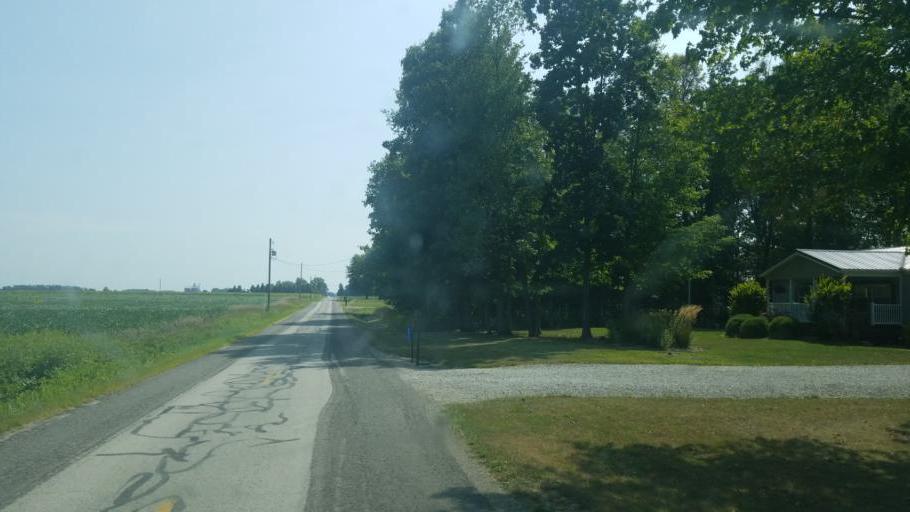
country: US
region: Ohio
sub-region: Crawford County
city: Crestline
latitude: 40.8534
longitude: -82.7443
